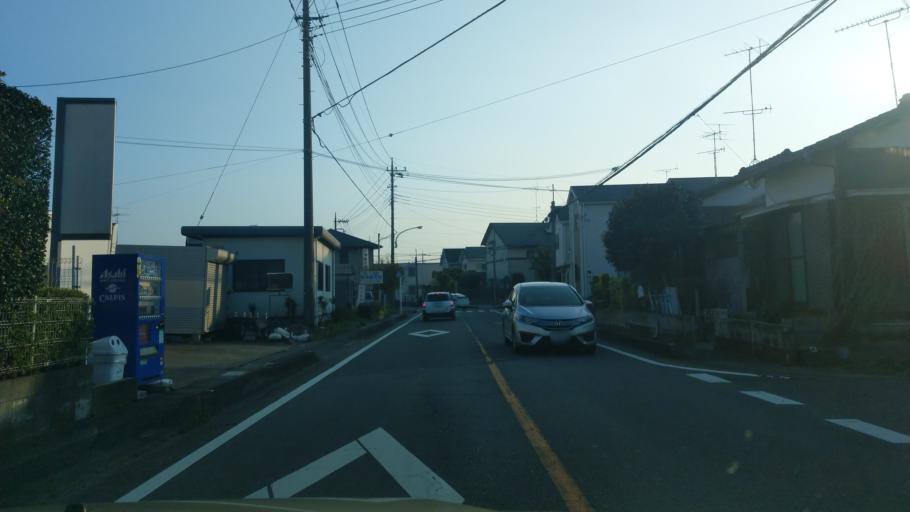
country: JP
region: Saitama
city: Ageoshimo
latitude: 36.0046
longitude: 139.6061
